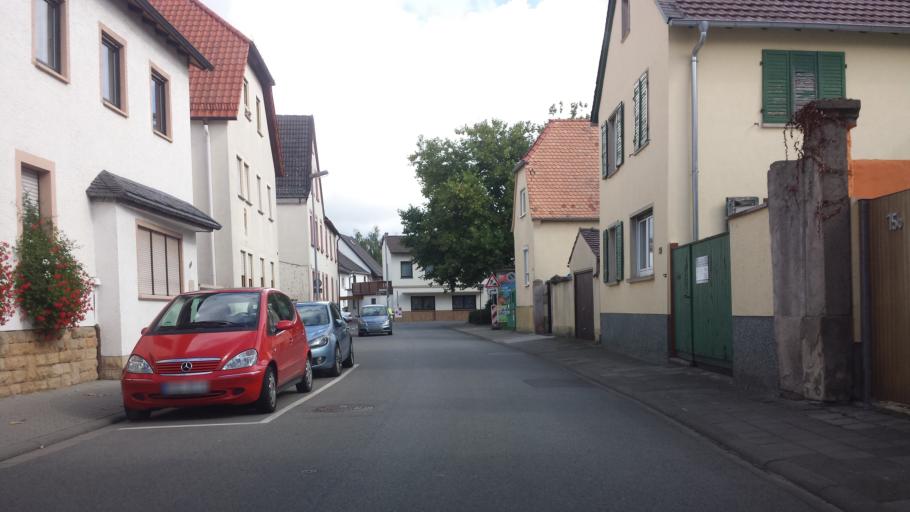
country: DE
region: Rheinland-Pfalz
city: Rodersheim-Gronau
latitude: 49.4301
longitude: 8.2558
